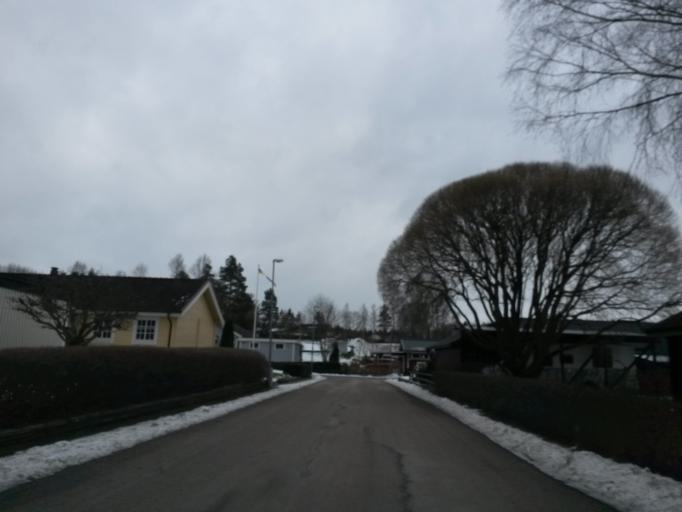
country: SE
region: Vaestra Goetaland
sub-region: Herrljunga Kommun
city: Herrljunga
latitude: 58.0778
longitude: 13.0432
